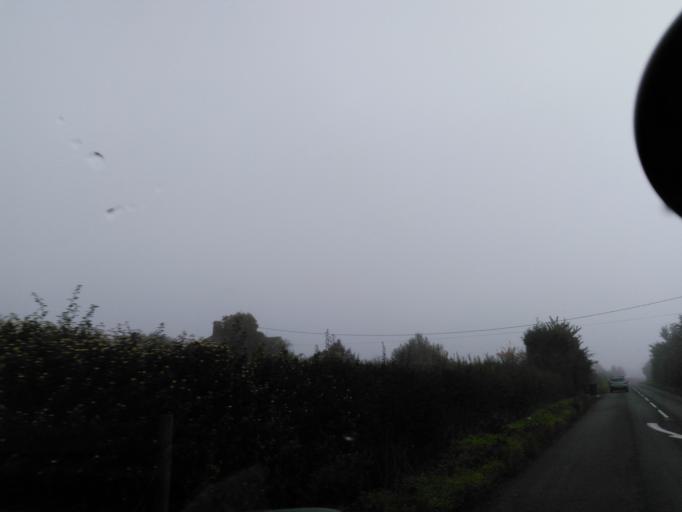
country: GB
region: England
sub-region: Wiltshire
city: Seend
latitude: 51.3586
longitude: -2.0942
